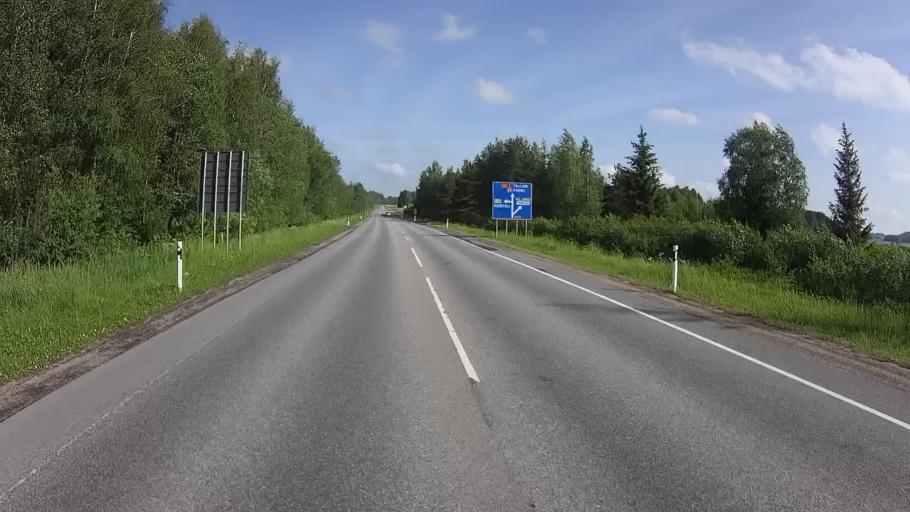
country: EE
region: Viljandimaa
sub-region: Viljandi linn
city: Viljandi
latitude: 58.3326
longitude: 25.5744
